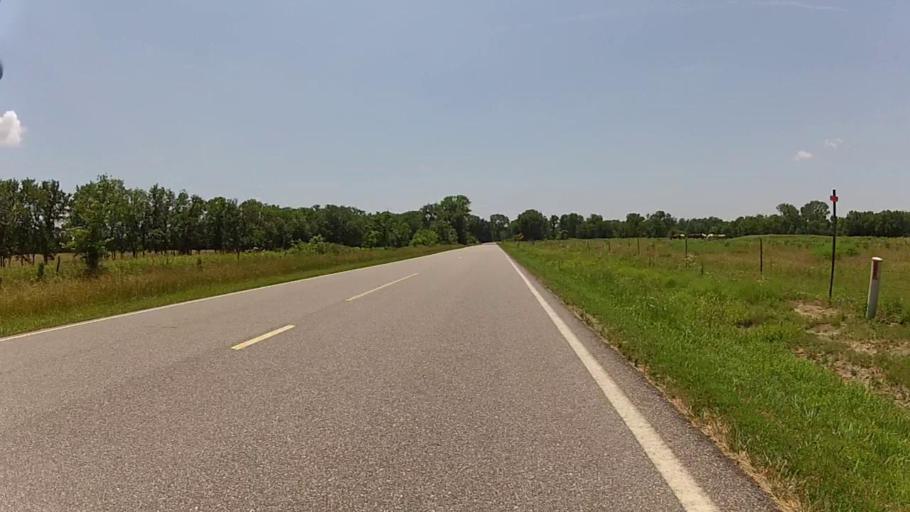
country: US
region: Kansas
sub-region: Montgomery County
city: Cherryvale
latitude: 37.2172
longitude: -95.5384
